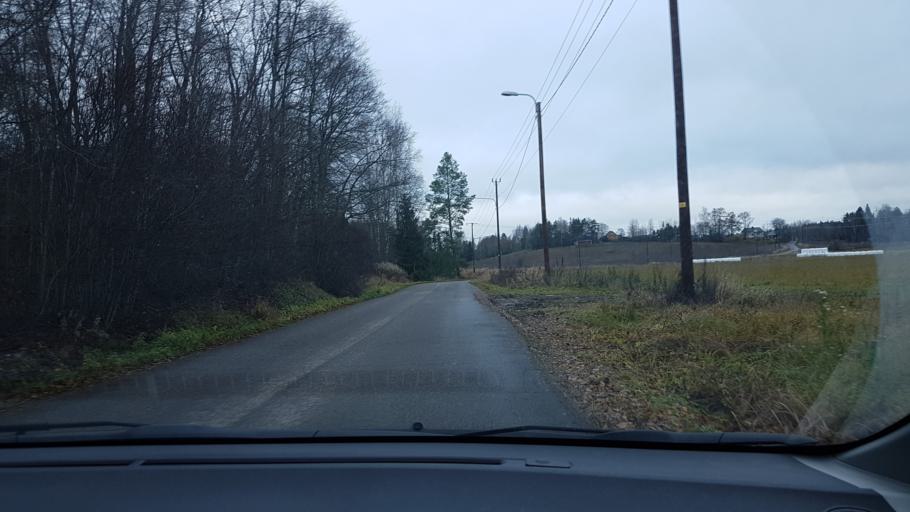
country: FI
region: Uusimaa
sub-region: Helsinki
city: Vantaa
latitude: 60.2781
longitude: 25.1366
